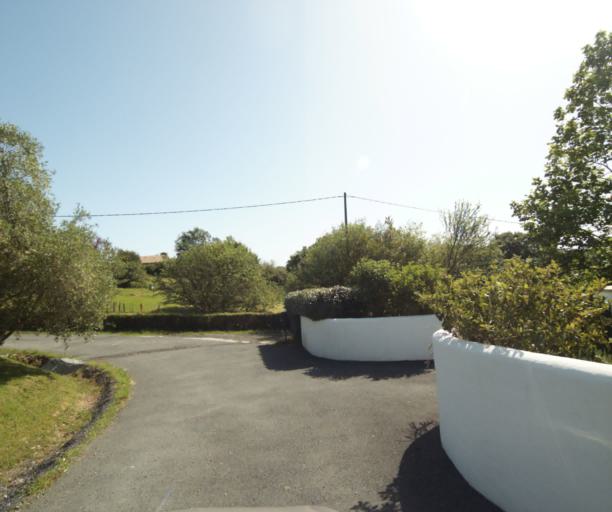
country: FR
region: Aquitaine
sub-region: Departement des Pyrenees-Atlantiques
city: Villefranque
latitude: 43.4536
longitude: -1.4407
